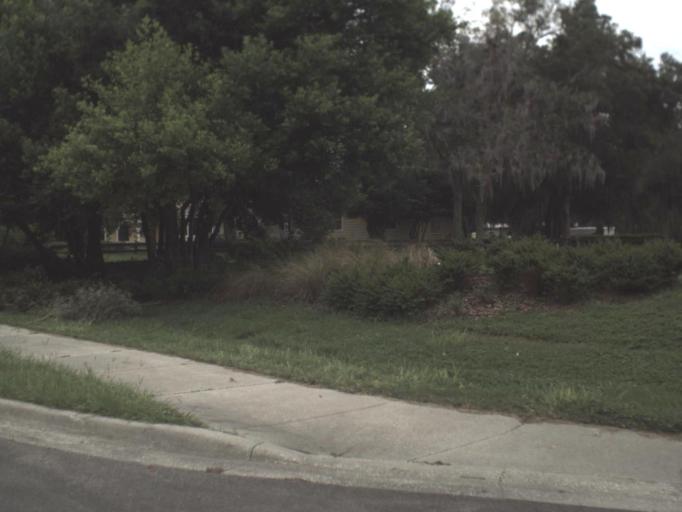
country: US
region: Florida
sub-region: Citrus County
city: Lecanto
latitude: 28.8789
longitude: -82.5355
